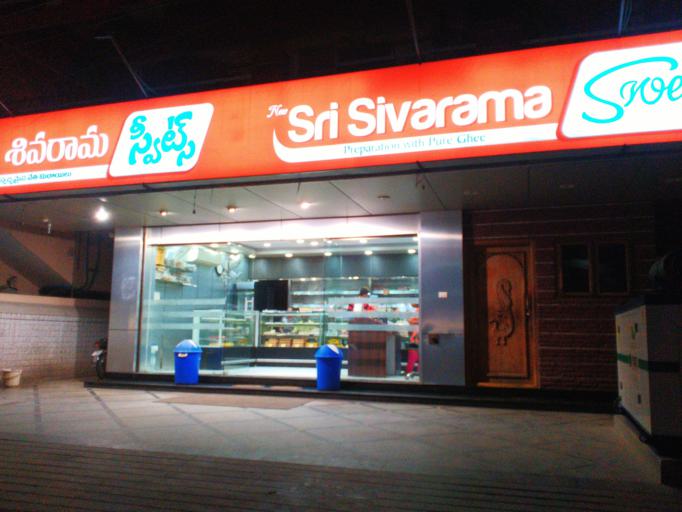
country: IN
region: Andhra Pradesh
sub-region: Vishakhapatnam
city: Yarada
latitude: 17.7415
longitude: 83.3337
